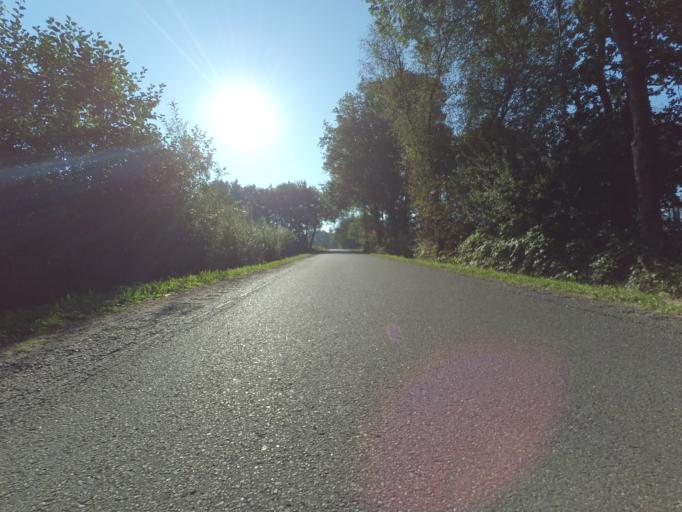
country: NL
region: Gelderland
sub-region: Gemeente Barneveld
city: Voorthuizen
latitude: 52.1910
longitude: 5.5657
